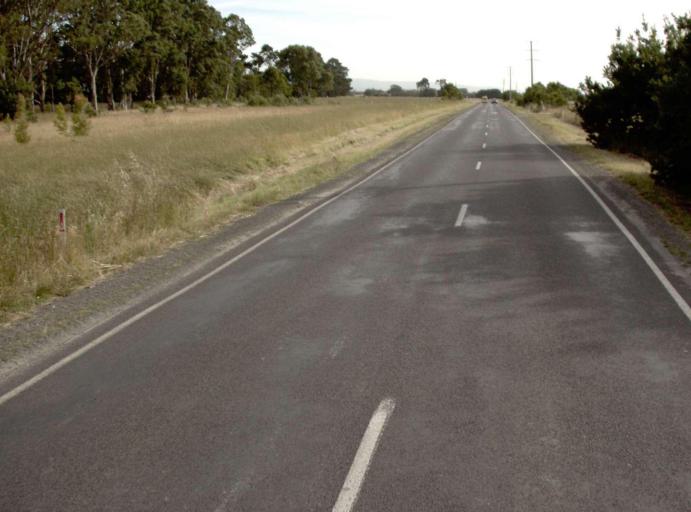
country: AU
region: Victoria
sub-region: Latrobe
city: Traralgon
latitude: -38.0975
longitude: 146.5965
